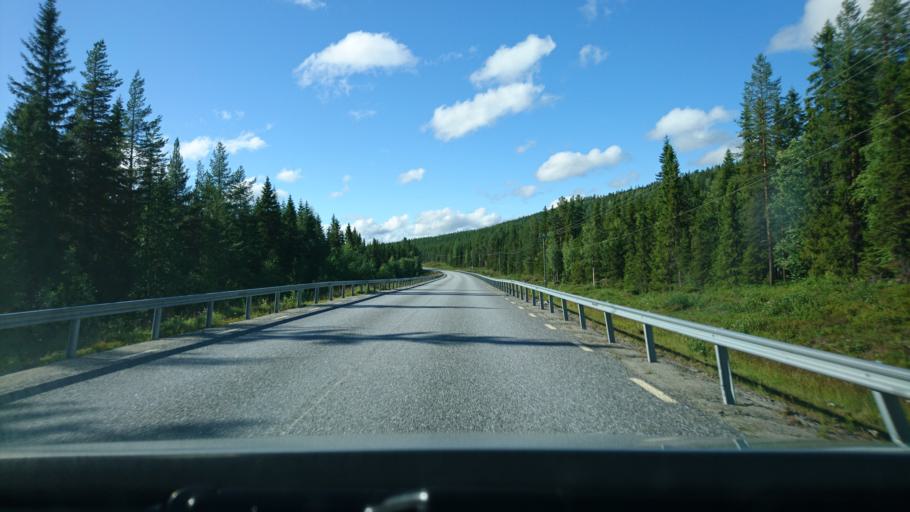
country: SE
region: Vaesterbotten
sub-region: Asele Kommun
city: Asele
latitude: 64.3577
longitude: 16.9707
